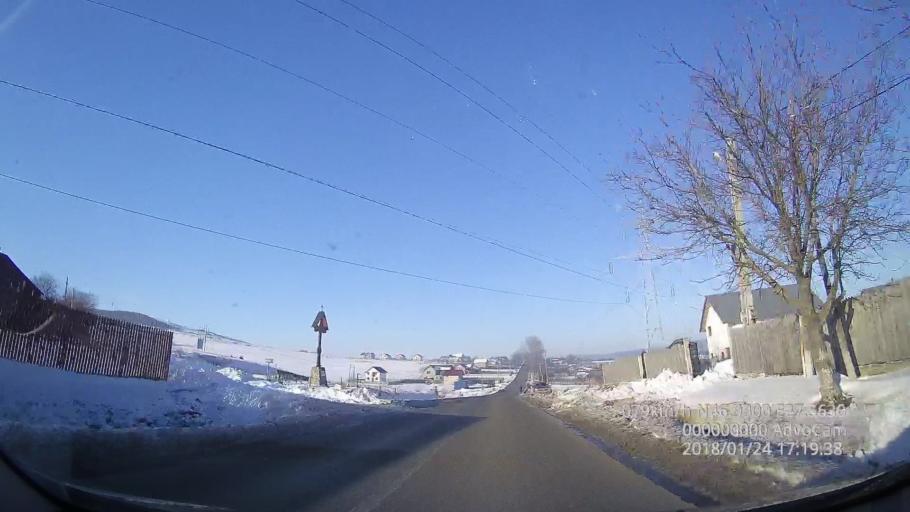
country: RO
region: Iasi
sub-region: Comuna Scanteia
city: Scanteia
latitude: 46.9305
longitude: 27.5629
